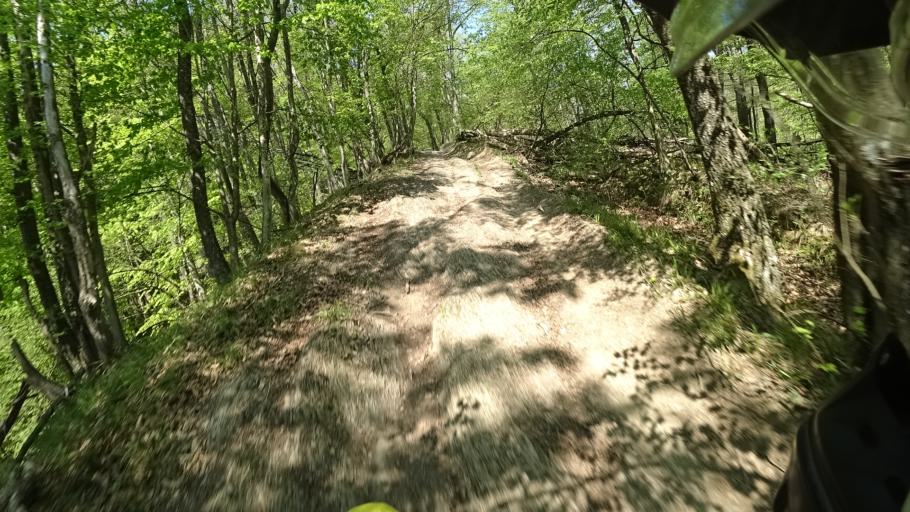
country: HR
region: Zagrebacka
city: Jablanovec
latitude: 45.8678
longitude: 15.9025
